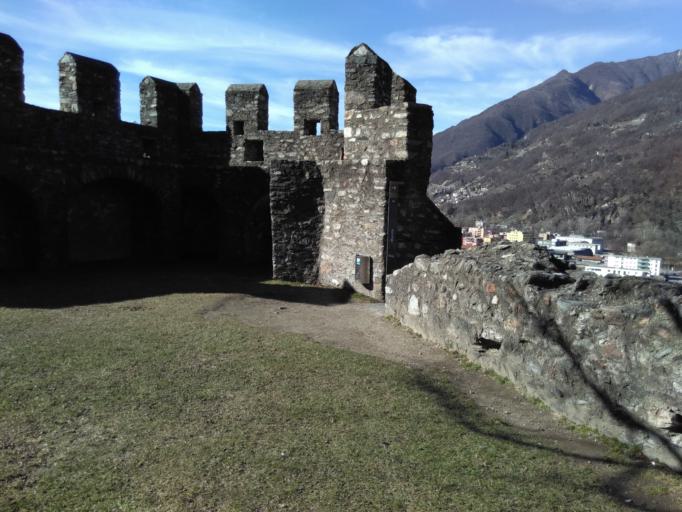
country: CH
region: Ticino
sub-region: Bellinzona District
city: Bellinzona
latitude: 46.1930
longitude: 9.0214
